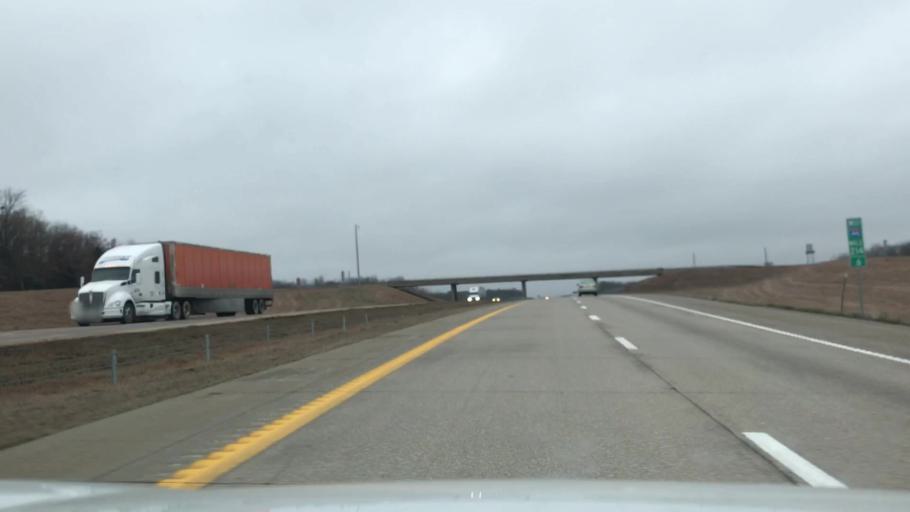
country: US
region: Missouri
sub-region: Crawford County
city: Bourbon
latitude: 38.1210
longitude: -91.3126
